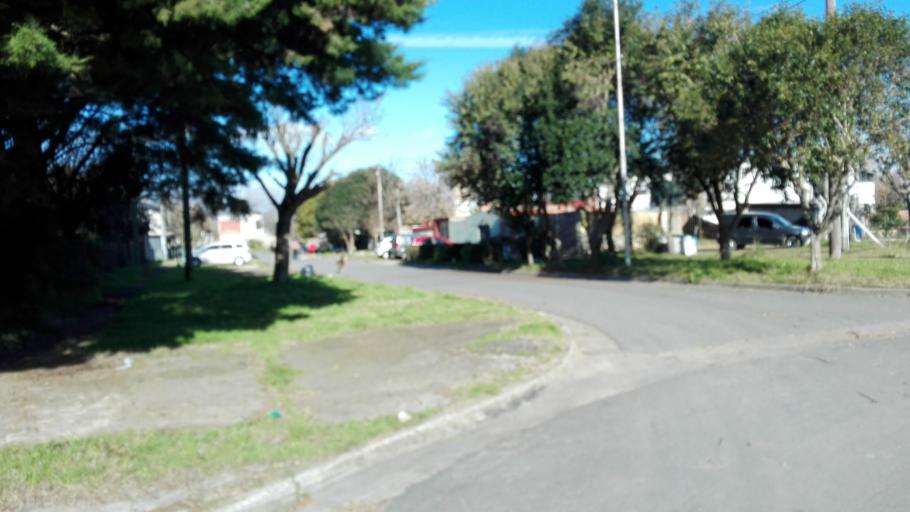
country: AR
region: Buenos Aires
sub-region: Partido de La Plata
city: La Plata
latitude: -34.8803
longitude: -57.9982
